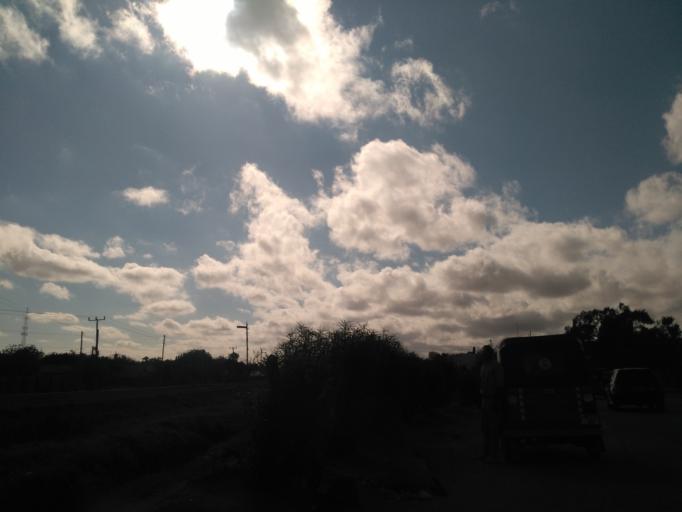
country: TZ
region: Dodoma
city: Dodoma
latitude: -6.1829
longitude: 35.7422
